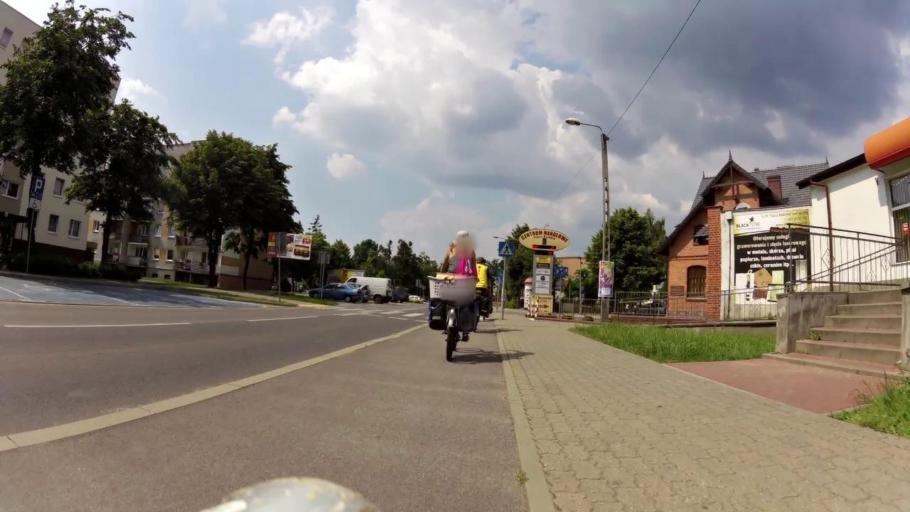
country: PL
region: Kujawsko-Pomorskie
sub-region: Powiat bydgoski
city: Koronowo
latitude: 53.3088
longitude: 17.9414
